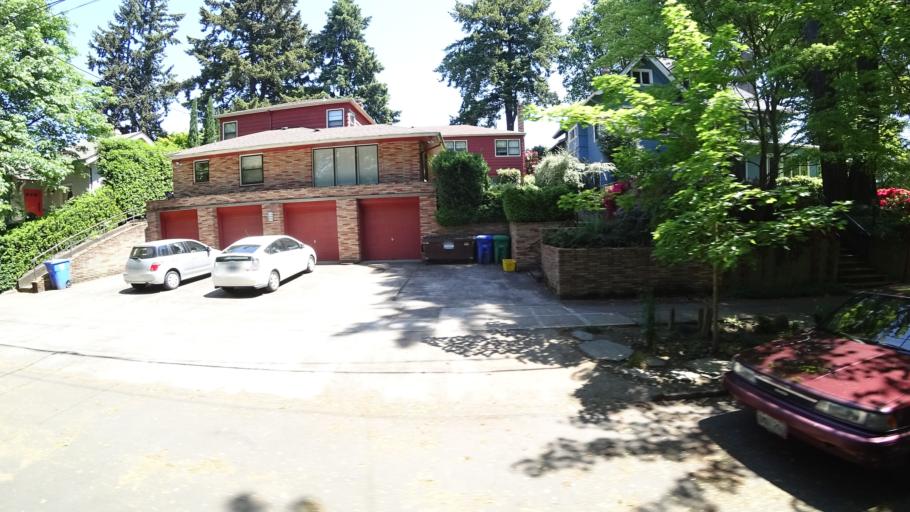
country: US
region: Oregon
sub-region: Multnomah County
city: Portland
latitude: 45.5381
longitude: -122.6453
